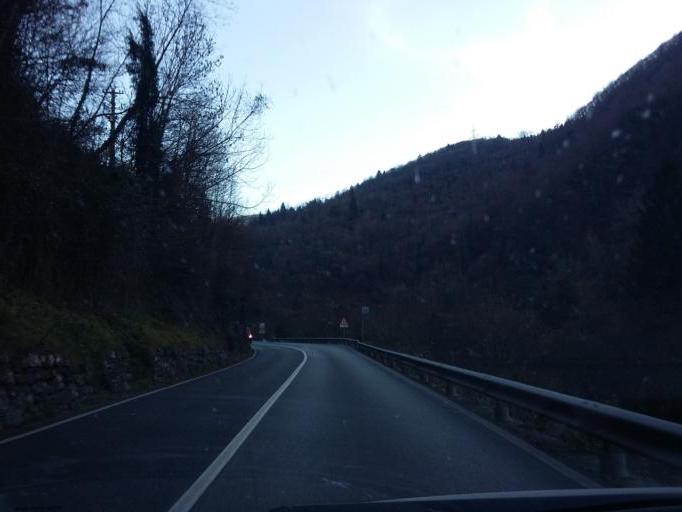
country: IT
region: Lombardy
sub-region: Provincia di Brescia
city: Lavenone
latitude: 45.7366
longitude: 10.4473
